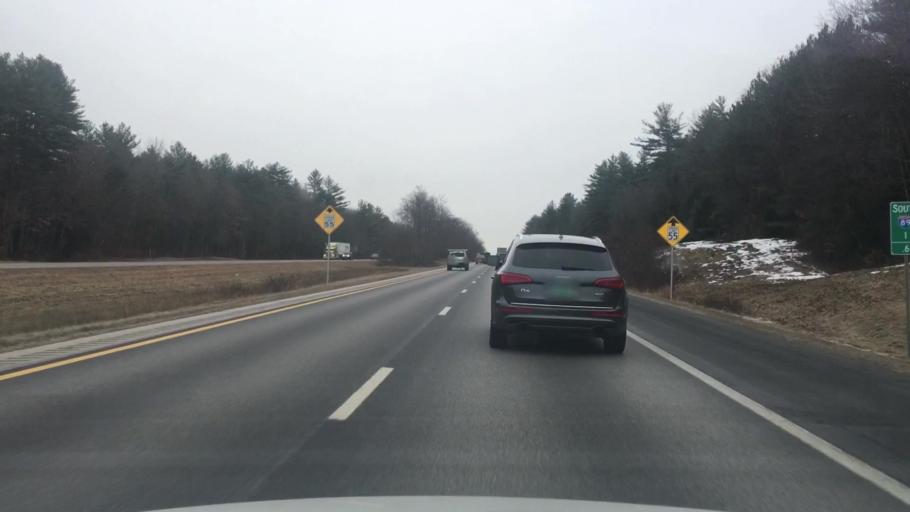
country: US
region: New Hampshire
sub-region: Merrimack County
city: Concord
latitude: 43.1758
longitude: -71.5589
